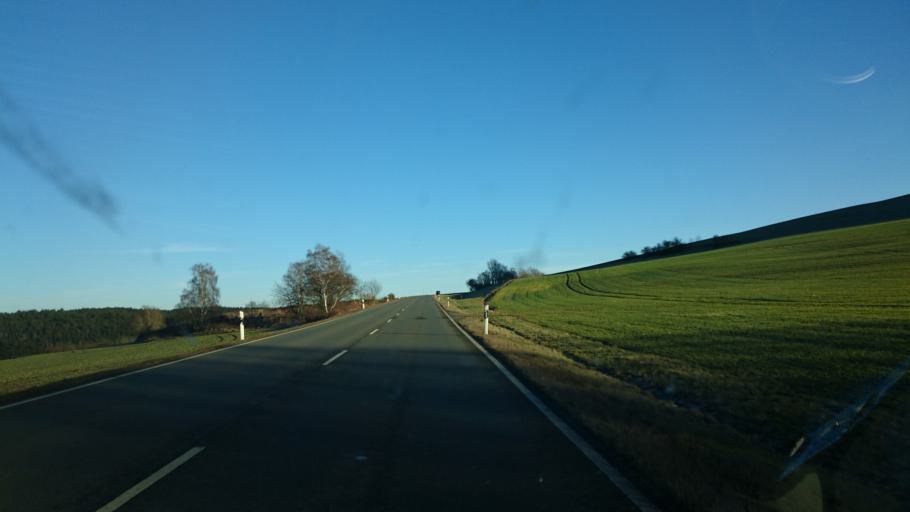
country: DE
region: Thuringia
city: Schleiz
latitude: 50.5816
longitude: 11.8333
